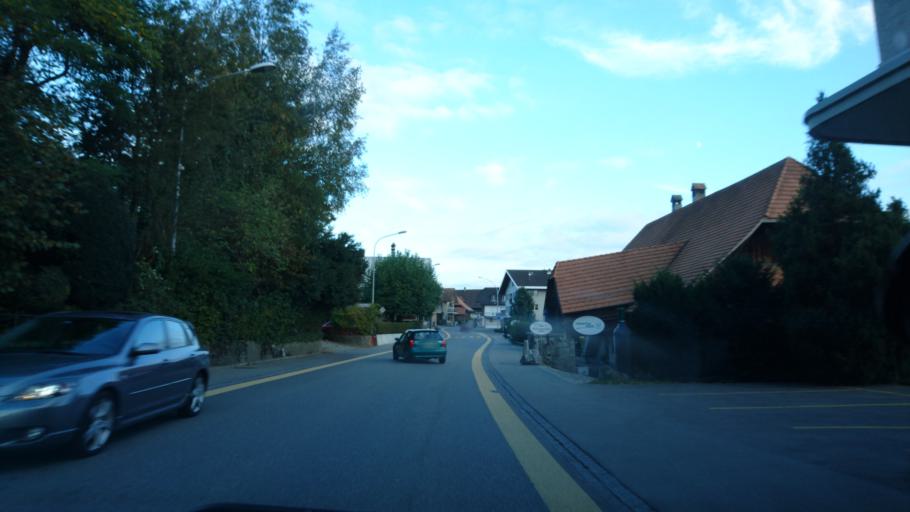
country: CH
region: Bern
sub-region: Bern-Mittelland District
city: Zaziwil
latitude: 46.9061
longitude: 7.6403
